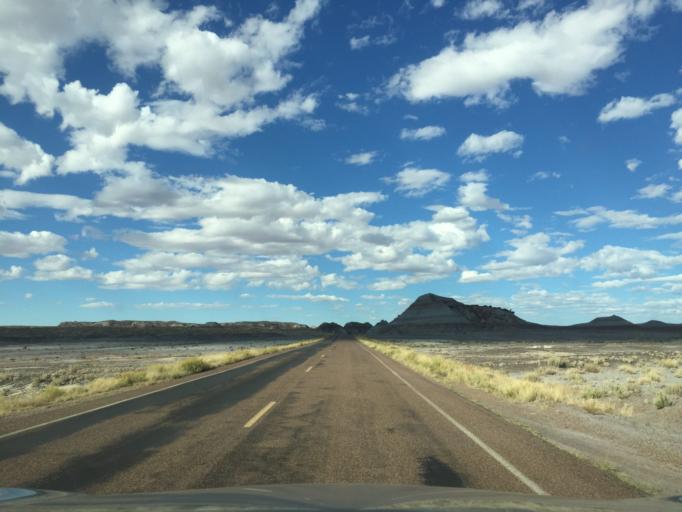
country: US
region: Arizona
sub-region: Navajo County
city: Holbrook
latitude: 34.9382
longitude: -109.7803
